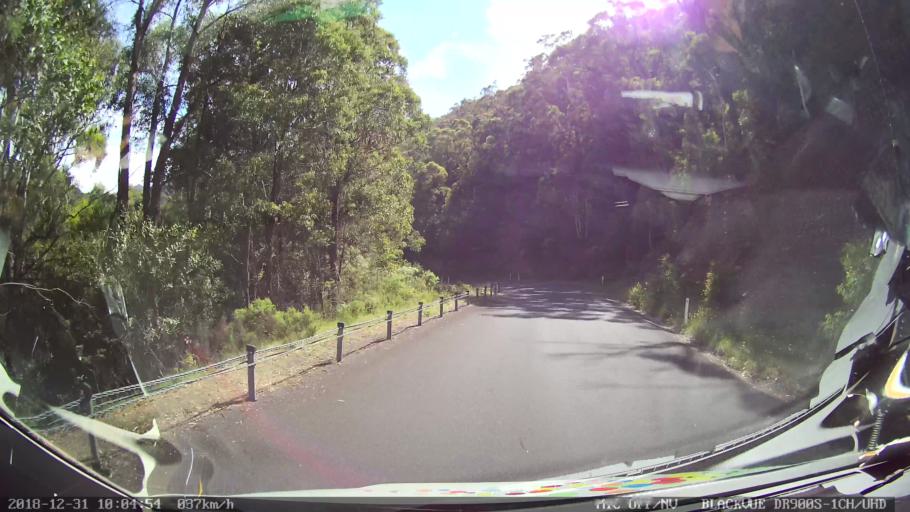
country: AU
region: New South Wales
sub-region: Snowy River
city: Jindabyne
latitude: -36.5289
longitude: 148.1927
